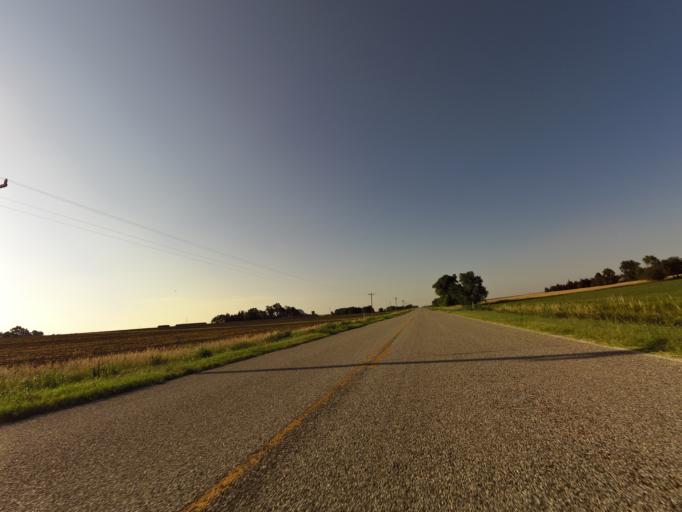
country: US
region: Kansas
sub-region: McPherson County
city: Inman
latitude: 38.1851
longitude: -97.8485
